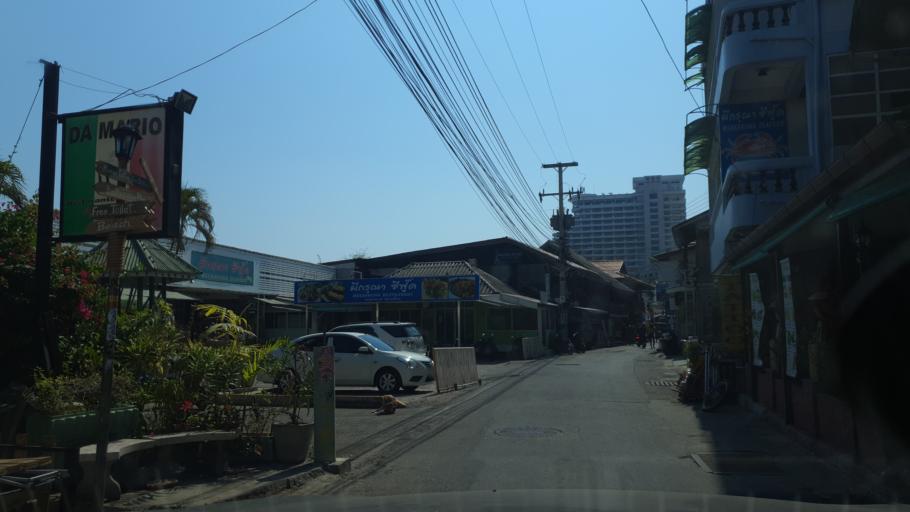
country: TH
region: Prachuap Khiri Khan
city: Hua Hin
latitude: 12.5737
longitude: 99.9592
